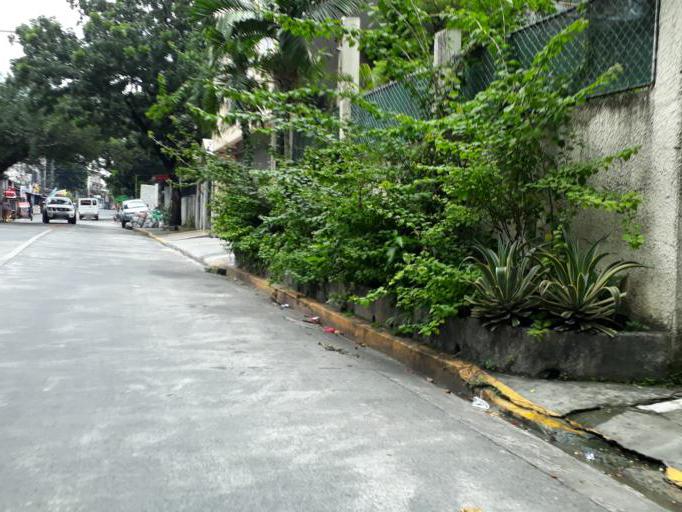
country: PH
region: Metro Manila
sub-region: City of Manila
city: Manila
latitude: 14.6111
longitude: 121.0002
